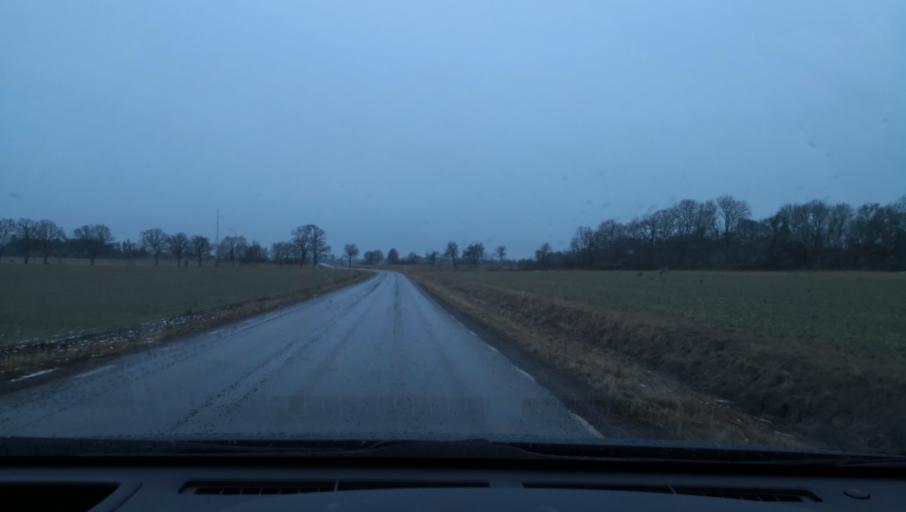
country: SE
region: Soedermanland
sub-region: Eskilstuna Kommun
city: Arla
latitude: 59.4459
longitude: 16.7216
